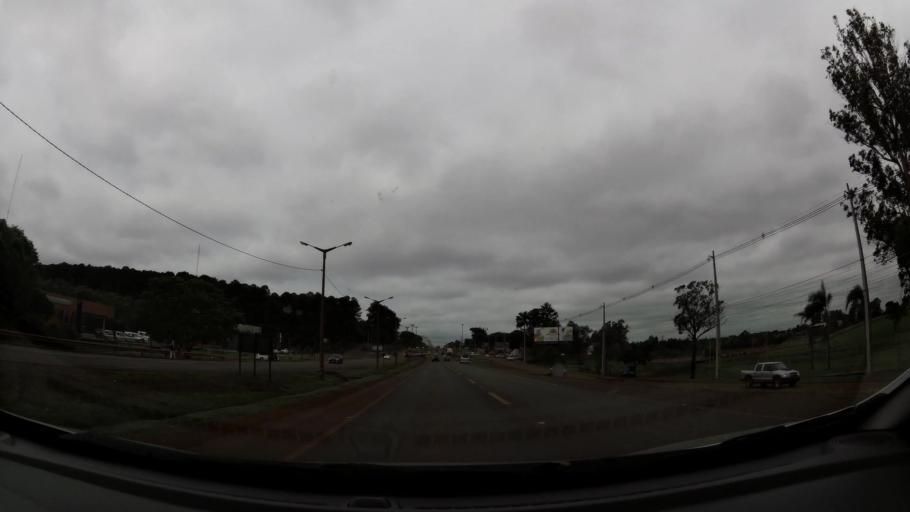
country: PY
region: Alto Parana
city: Ciudad del Este
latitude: -25.4949
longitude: -54.7013
